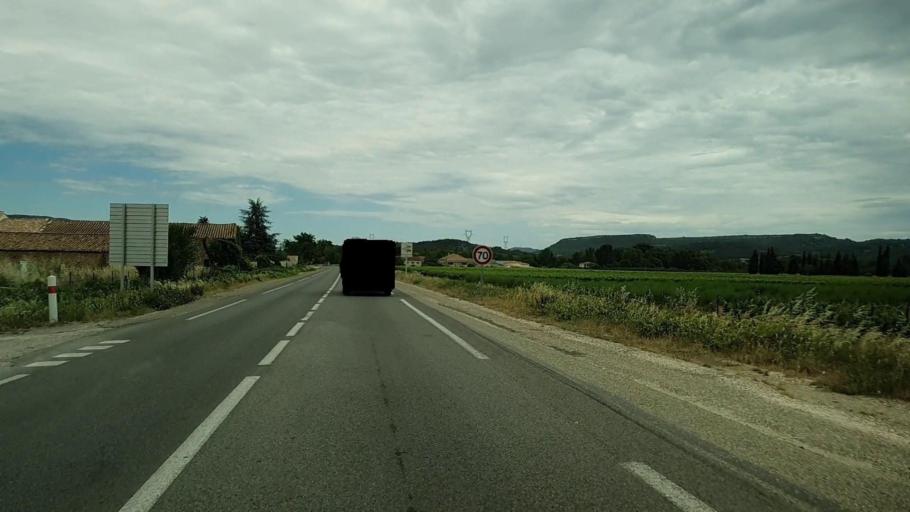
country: FR
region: Languedoc-Roussillon
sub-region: Departement du Gard
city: Connaux
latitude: 44.0893
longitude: 4.5961
